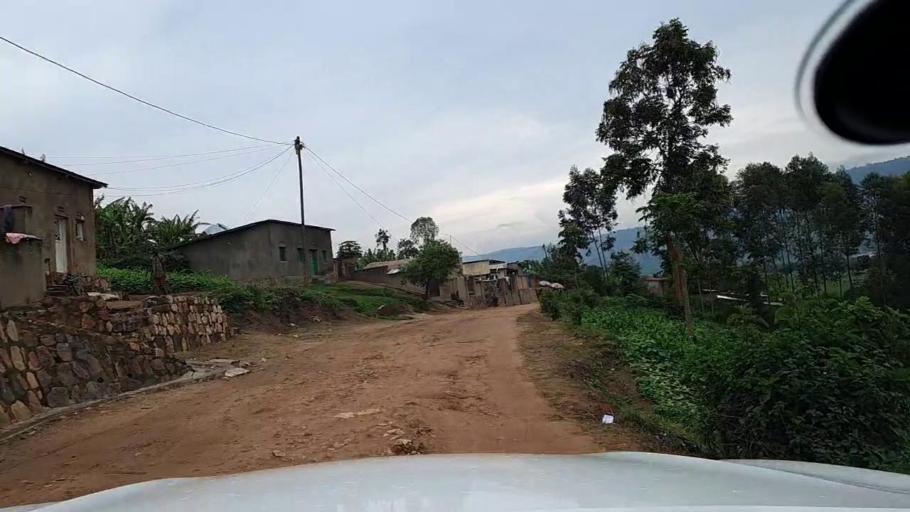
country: RW
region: Kigali
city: Kigali
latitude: -1.9579
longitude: 29.9960
